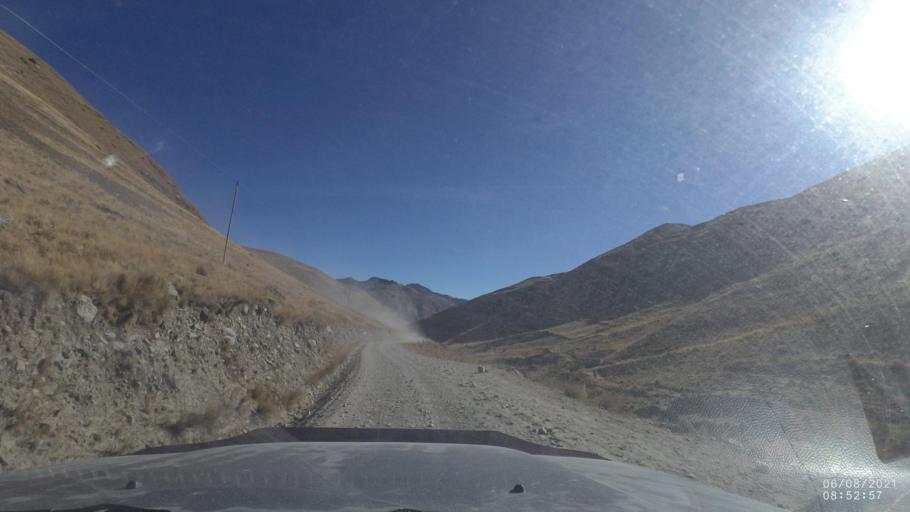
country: BO
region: Cochabamba
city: Sipe Sipe
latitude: -17.1333
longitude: -66.4397
